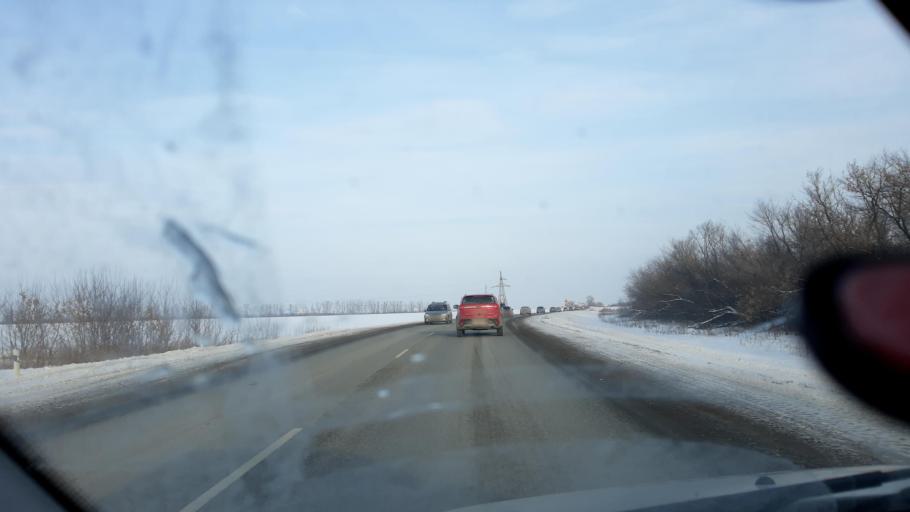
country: RU
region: Bashkortostan
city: Chishmy
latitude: 54.5436
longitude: 55.3214
